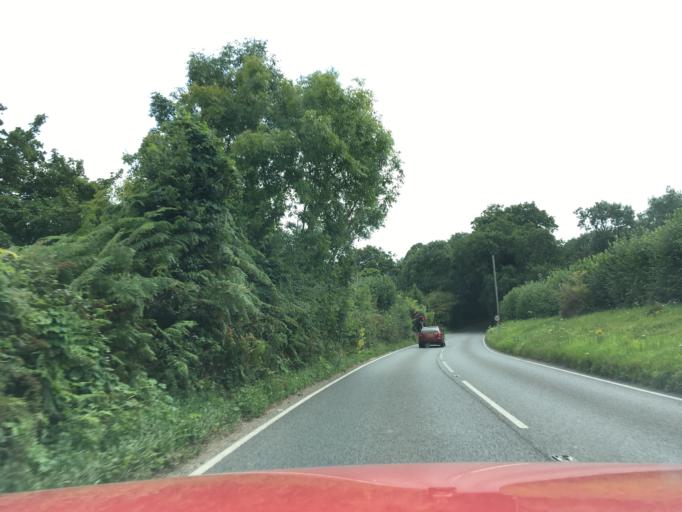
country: GB
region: England
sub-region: Kent
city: Royal Tunbridge Wells
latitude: 51.1244
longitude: 0.1945
